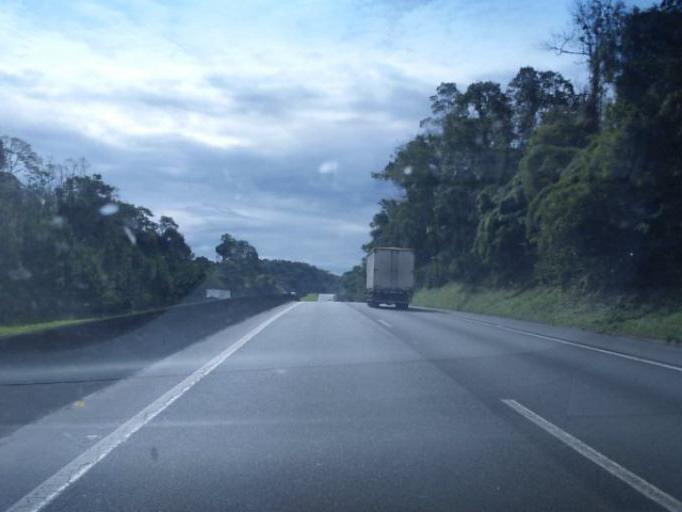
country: BR
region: Sao Paulo
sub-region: Cajati
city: Cajati
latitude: -24.9715
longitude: -48.3735
